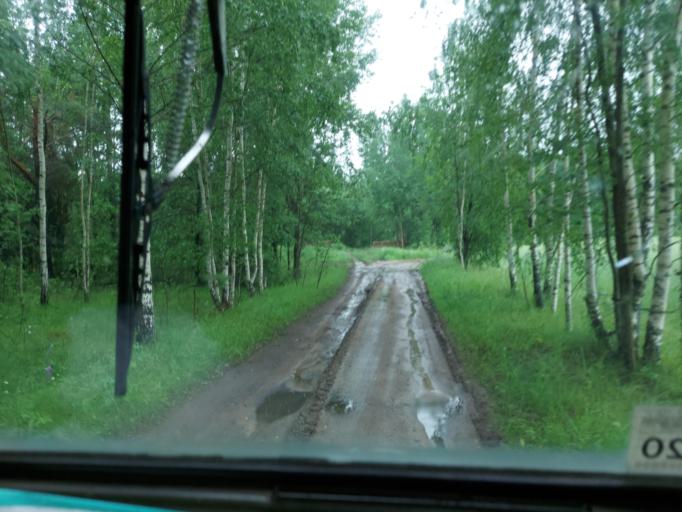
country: BY
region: Mogilev
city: Poselok Voskhod
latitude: 53.6727
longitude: 30.4034
